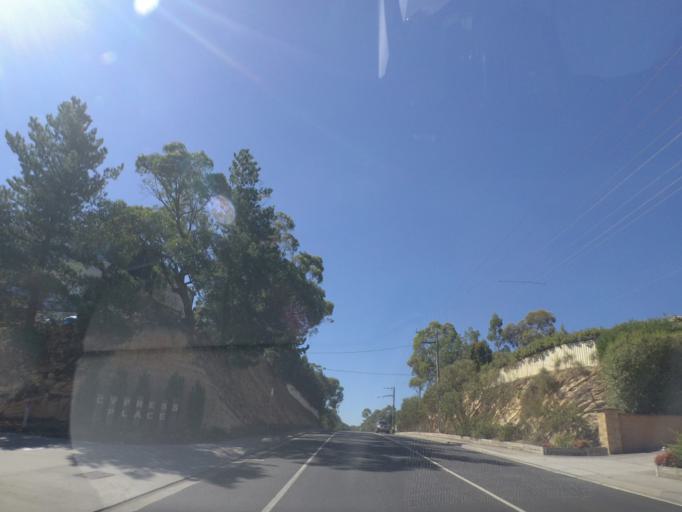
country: AU
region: Victoria
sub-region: Maroondah
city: Warranwood
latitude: -37.7821
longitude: 145.2489
